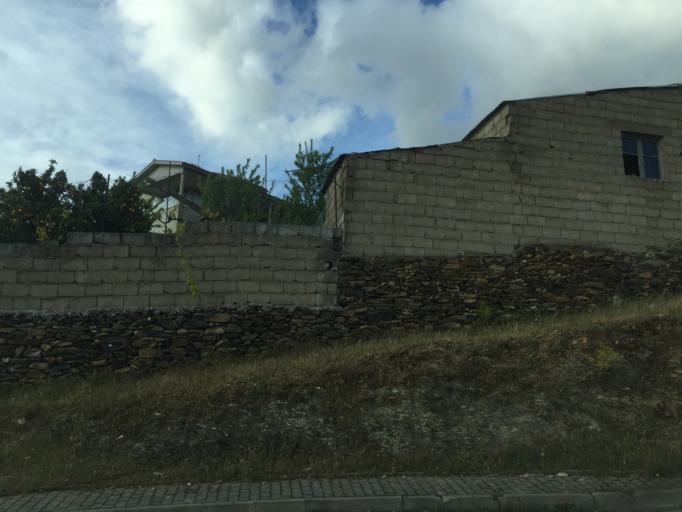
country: PT
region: Braganca
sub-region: Alfandega da Fe
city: Alfandega da Fe
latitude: 41.3406
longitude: -6.9669
